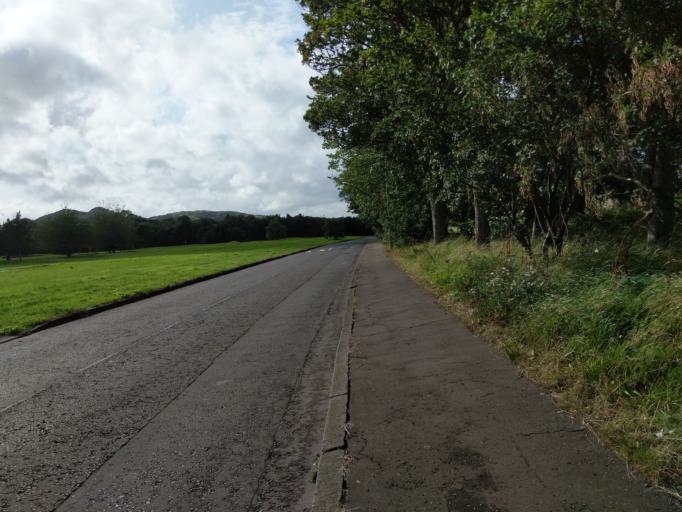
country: GB
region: Scotland
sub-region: West Lothian
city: Seafield
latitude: 55.9475
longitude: -3.1123
